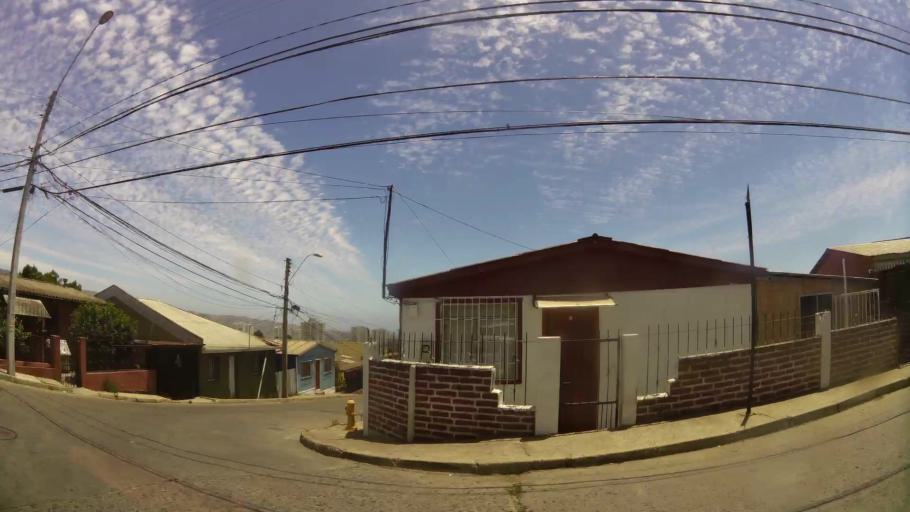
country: CL
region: Valparaiso
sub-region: Provincia de Valparaiso
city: Vina del Mar
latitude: -33.0446
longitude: -71.5815
